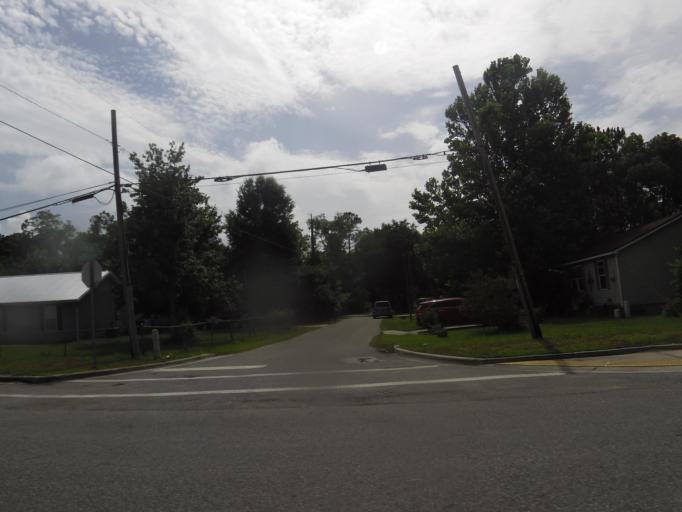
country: US
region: Florida
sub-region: Saint Johns County
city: Saint Augustine
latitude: 29.8963
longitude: -81.3452
